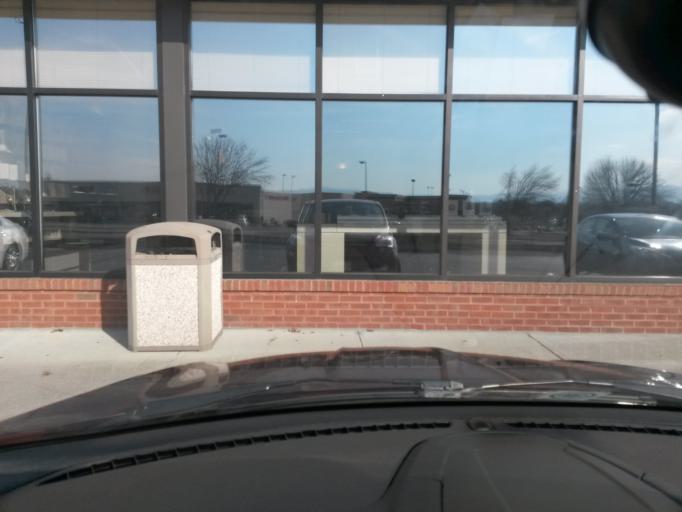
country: US
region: Virginia
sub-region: City of Roanoke
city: Roanoke
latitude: 37.3015
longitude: -79.9564
